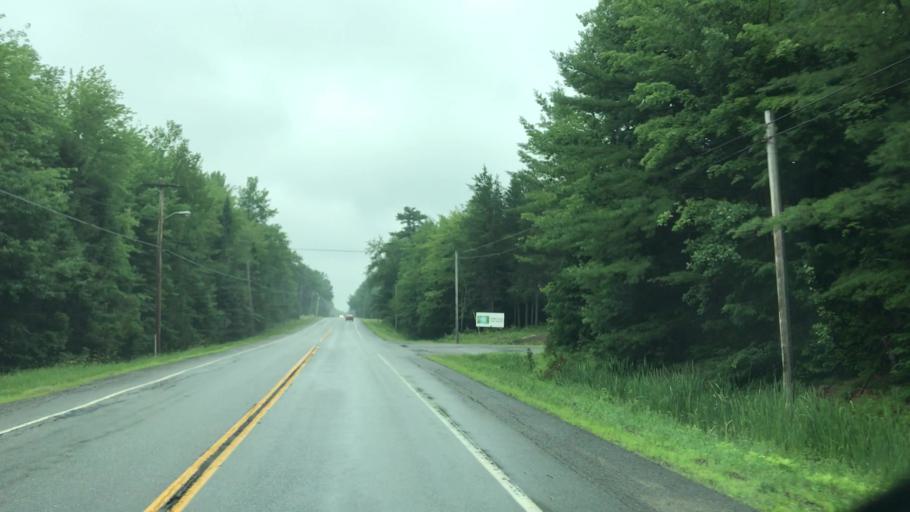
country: US
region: Maine
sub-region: Penobscot County
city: Howland
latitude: 45.2552
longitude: -68.6375
